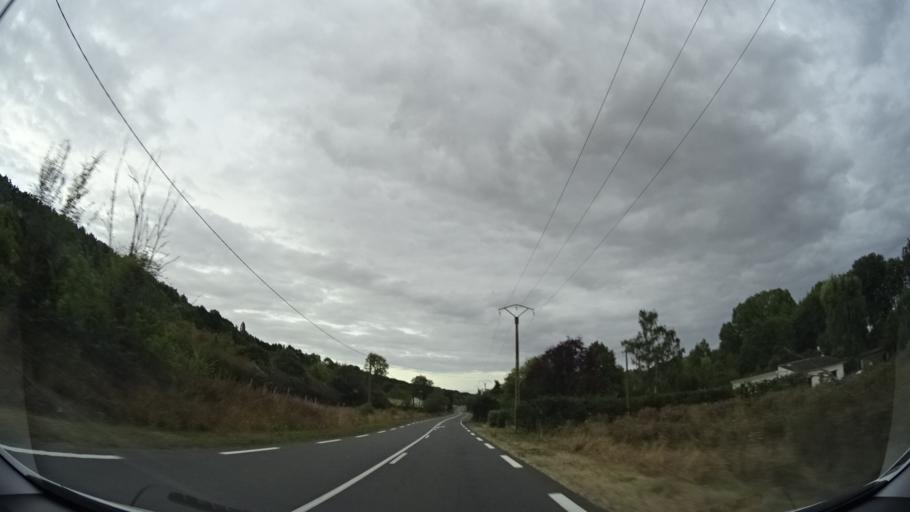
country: FR
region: Centre
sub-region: Departement du Loiret
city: Trigueres
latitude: 47.9448
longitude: 3.0118
